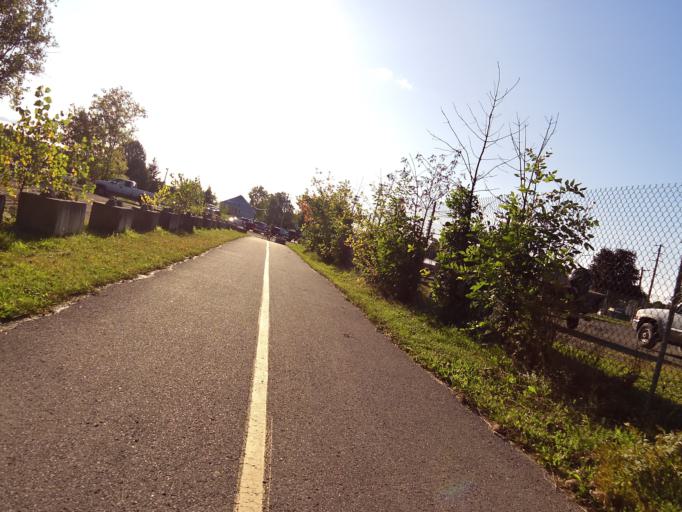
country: CA
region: Quebec
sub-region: Outaouais
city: Gatineau
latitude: 45.4769
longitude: -75.6387
